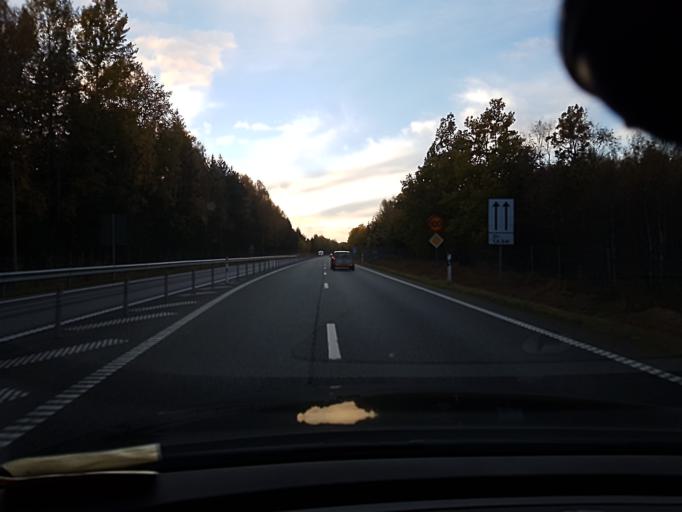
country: SE
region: Kronoberg
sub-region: Ljungby Kommun
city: Lagan
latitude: 56.8513
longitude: 14.0353
